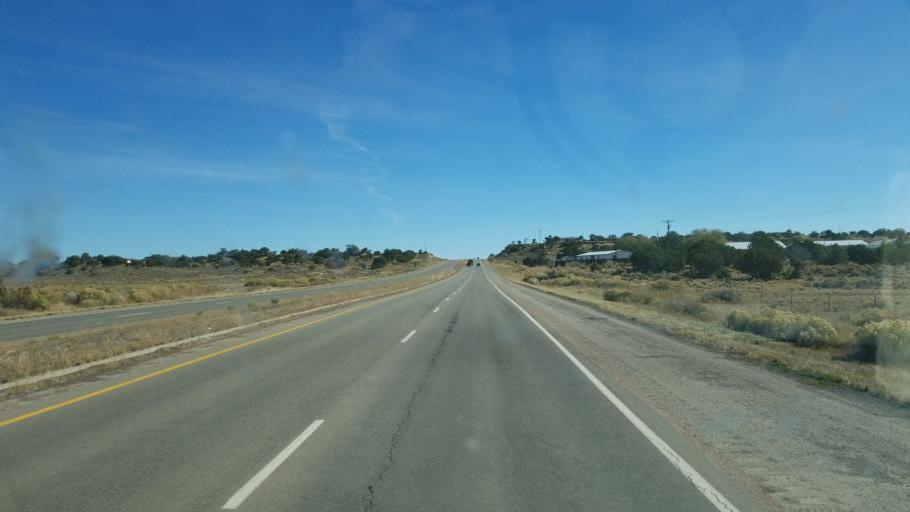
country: US
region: Arizona
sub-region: Apache County
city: Window Rock
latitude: 35.6313
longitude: -108.9092
